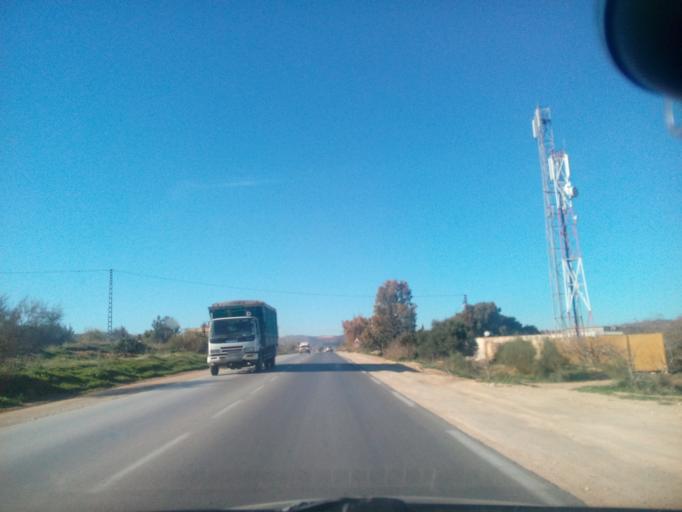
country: DZ
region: Relizane
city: Relizane
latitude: 35.9094
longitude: 0.5071
